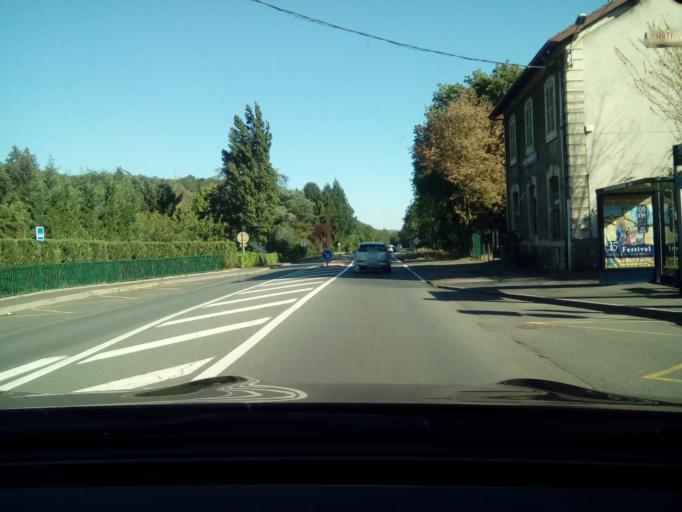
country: FR
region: Rhone-Alpes
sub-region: Departement du Rhone
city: Chessy
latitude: 45.8755
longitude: 4.6451
